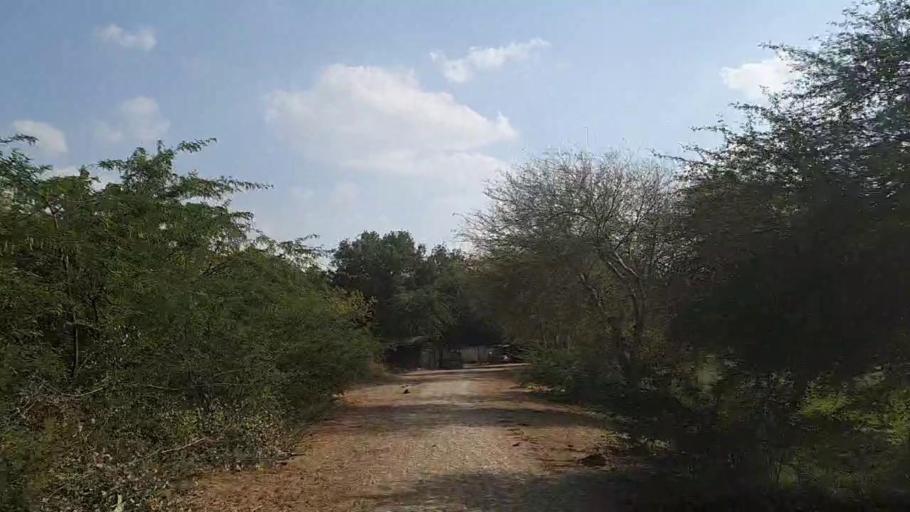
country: PK
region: Sindh
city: Jati
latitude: 24.4767
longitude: 68.3387
